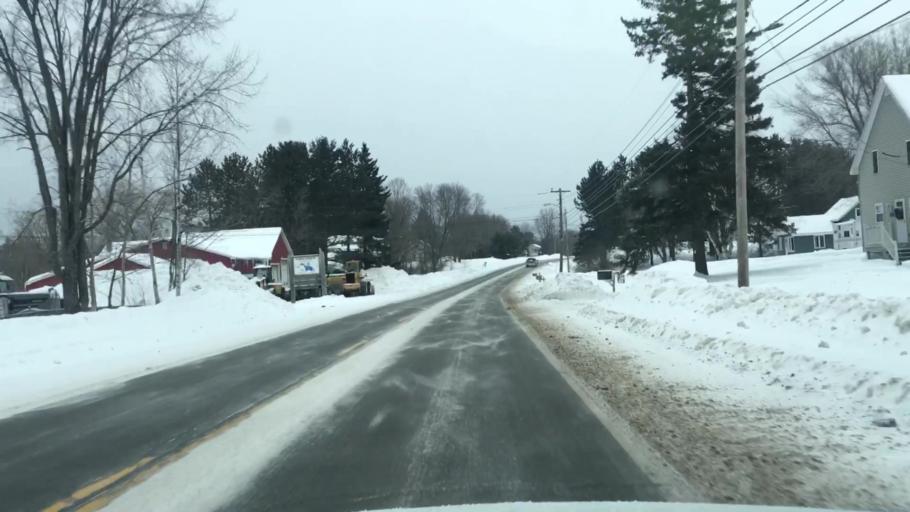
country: US
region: Maine
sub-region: Penobscot County
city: Lincoln
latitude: 45.4004
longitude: -68.4909
